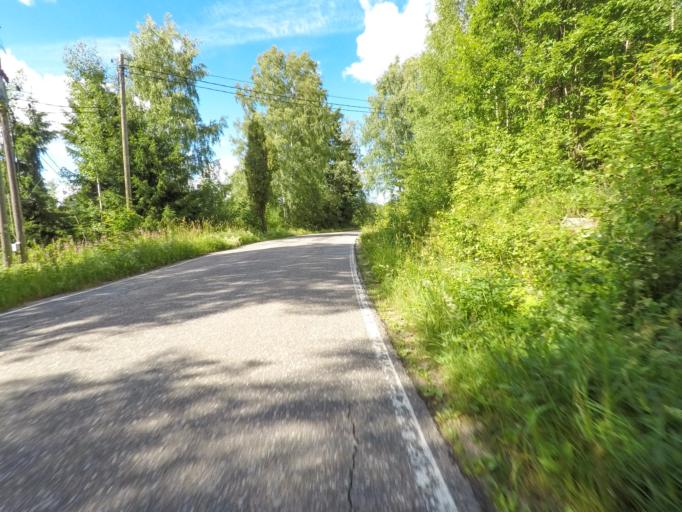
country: FI
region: South Karelia
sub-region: Lappeenranta
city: Joutseno
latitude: 61.1131
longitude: 28.3717
